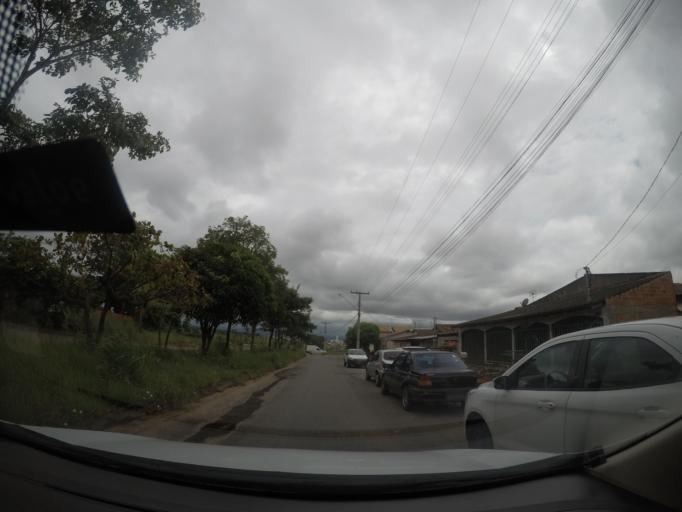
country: BR
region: Goias
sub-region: Goiania
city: Goiania
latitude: -16.7489
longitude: -49.3364
